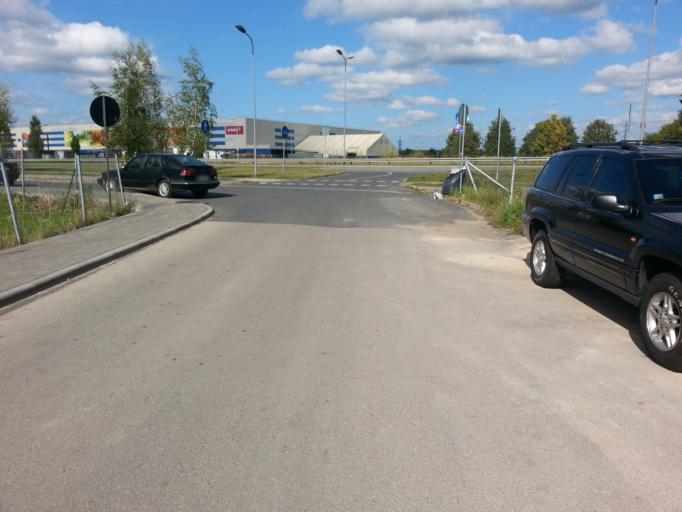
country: LV
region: Stopini
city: Ulbroka
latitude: 56.9431
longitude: 24.2281
